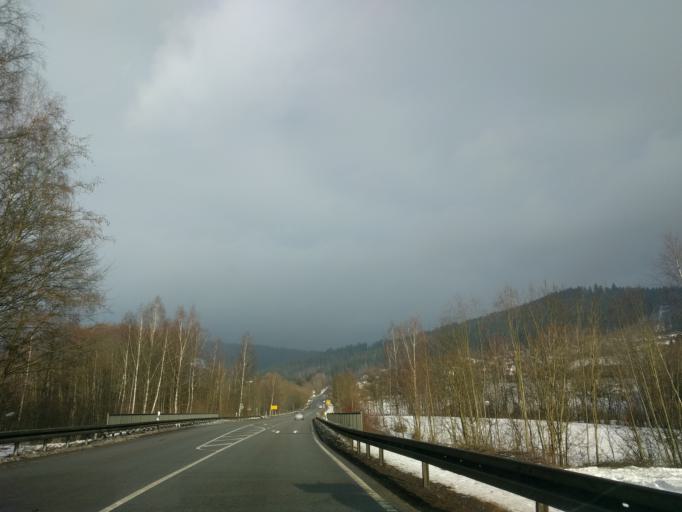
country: DE
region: Bavaria
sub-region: Lower Bavaria
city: Zwiesel
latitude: 49.0320
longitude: 13.2358
